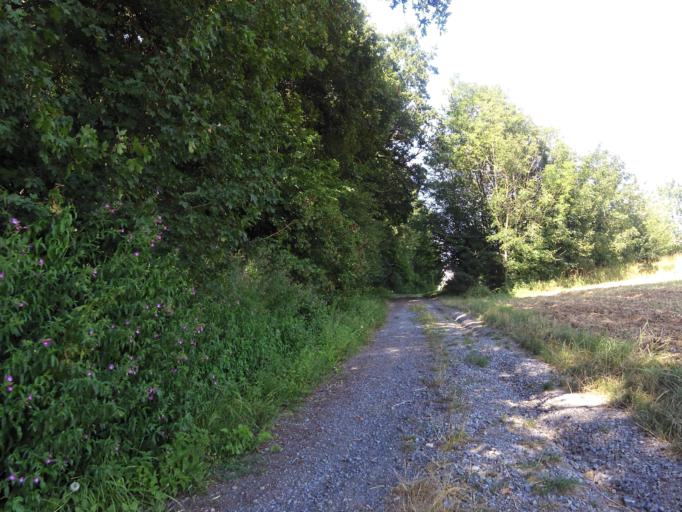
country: DE
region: Bavaria
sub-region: Regierungsbezirk Unterfranken
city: Estenfeld
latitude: 49.8321
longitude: 9.9829
